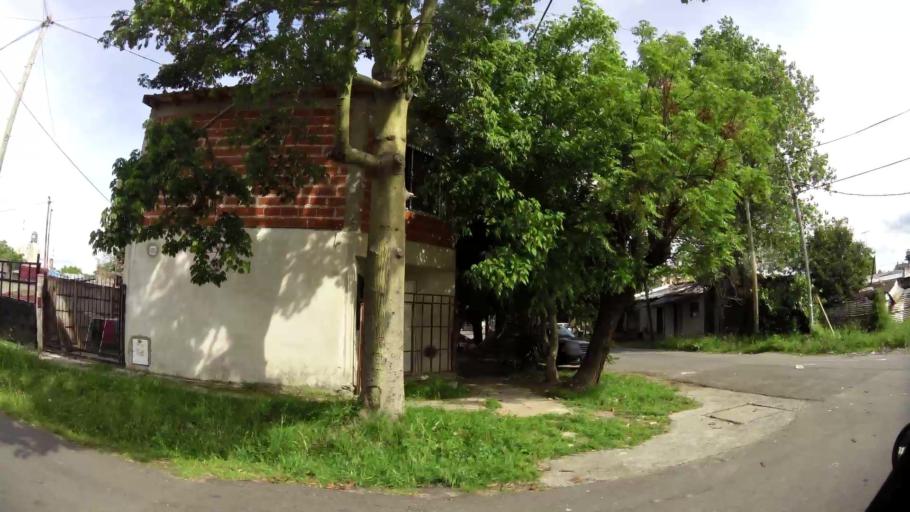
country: AR
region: Buenos Aires
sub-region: Partido de Quilmes
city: Quilmes
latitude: -34.7712
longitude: -58.2531
